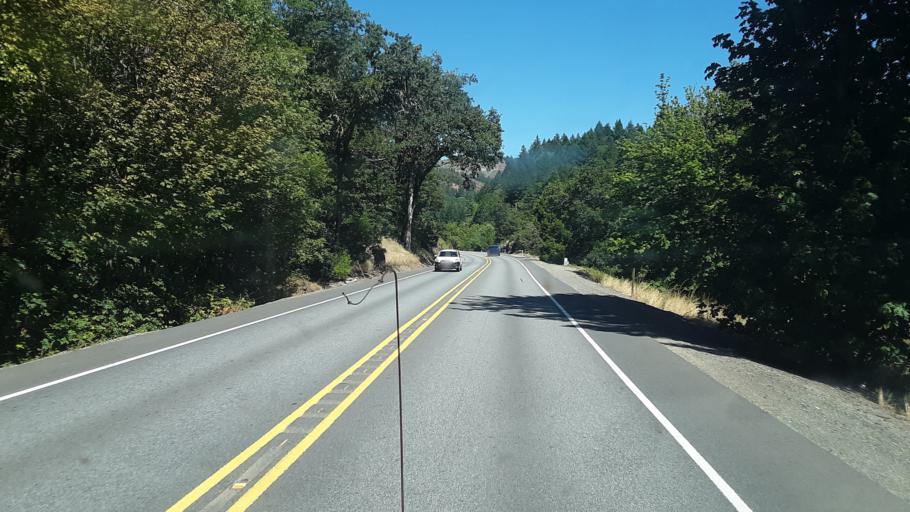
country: US
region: Oregon
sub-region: Josephine County
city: Redwood
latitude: 42.3625
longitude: -123.5209
